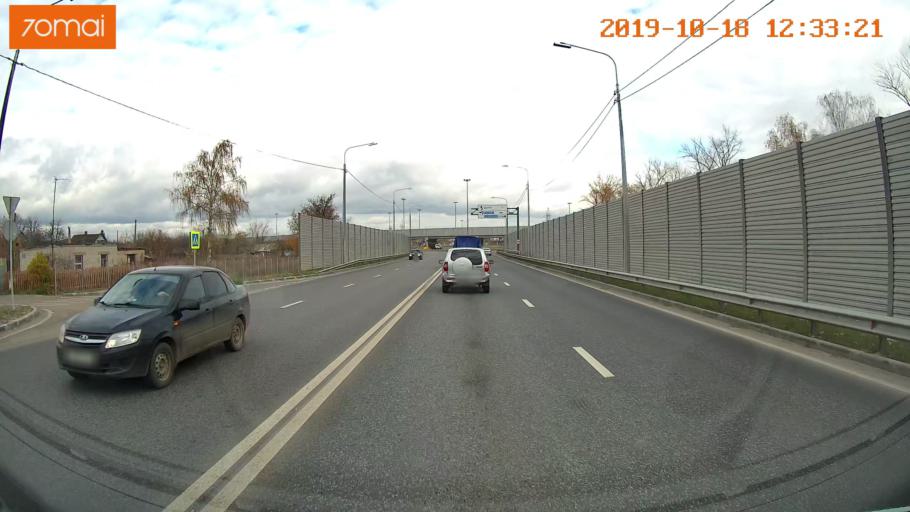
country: RU
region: Rjazan
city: Ryazan'
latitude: 54.6078
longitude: 39.6371
